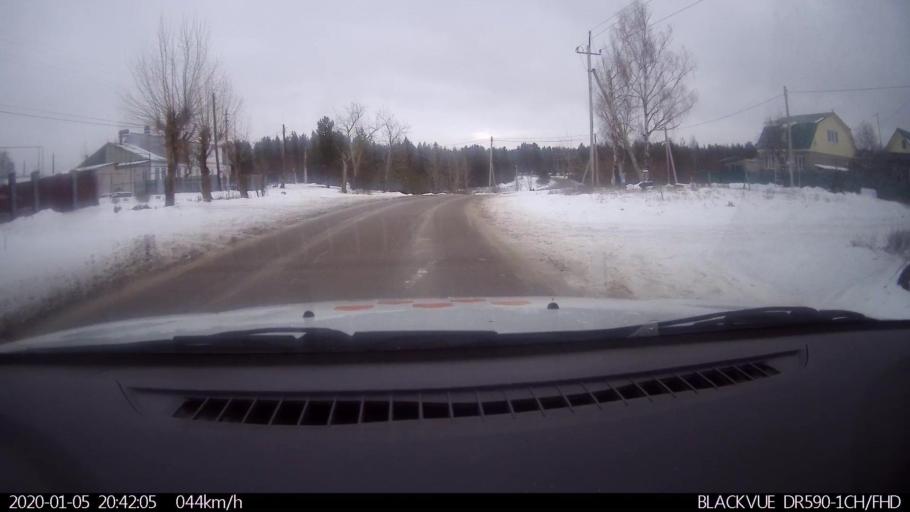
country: RU
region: Nizjnij Novgorod
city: Lukino
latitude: 56.3986
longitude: 43.7299
